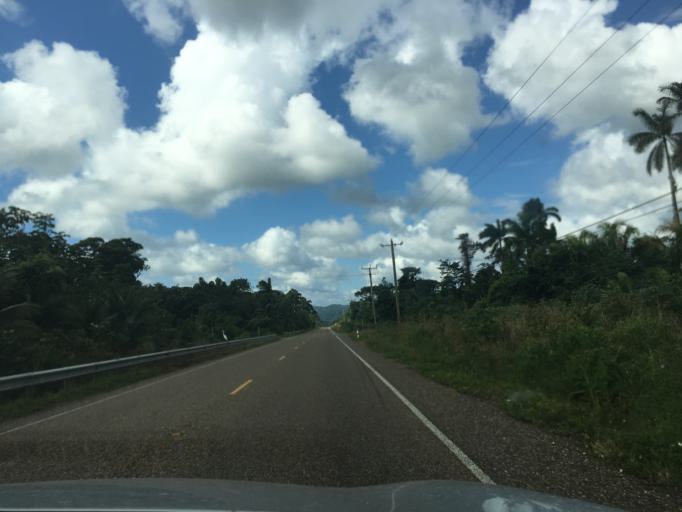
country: BZ
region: Stann Creek
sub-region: Dangriga
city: Dangriga
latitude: 16.8546
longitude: -88.3257
